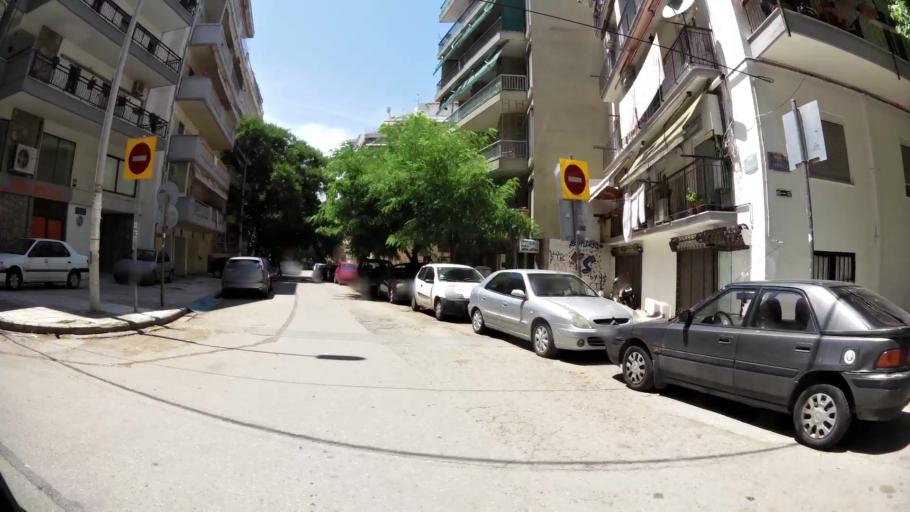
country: GR
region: Central Macedonia
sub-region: Nomos Thessalonikis
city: Triandria
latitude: 40.6126
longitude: 22.9590
